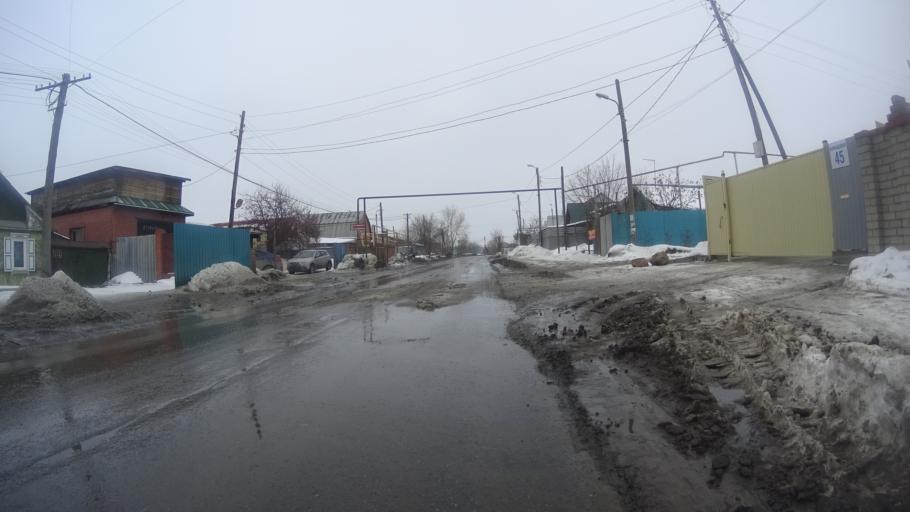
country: RU
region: Chelyabinsk
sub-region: Gorod Chelyabinsk
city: Chelyabinsk
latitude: 55.1305
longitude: 61.3964
